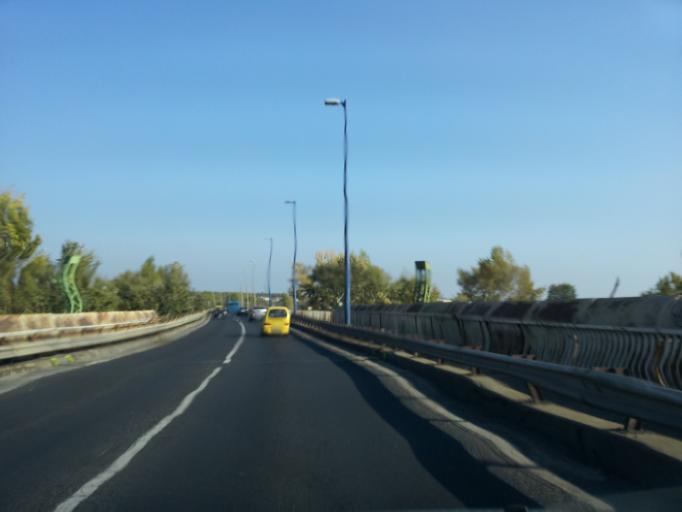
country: HU
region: Budapest
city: Budapest XIX. keruelet
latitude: 47.4612
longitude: 19.1608
